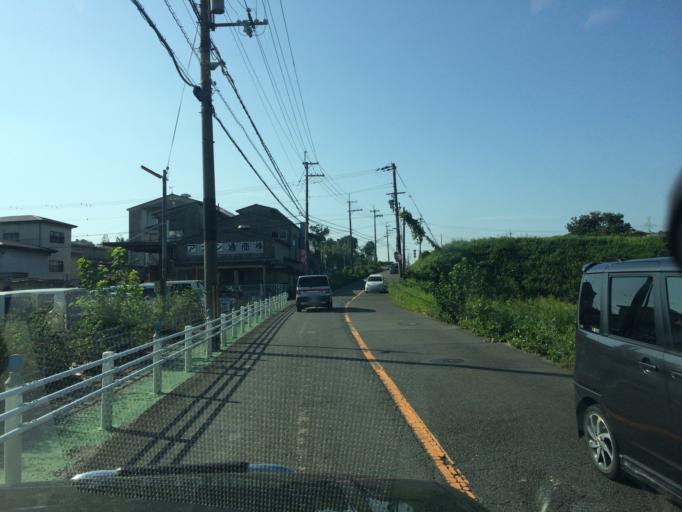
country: JP
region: Kyoto
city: Tanabe
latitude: 34.8087
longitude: 135.7887
